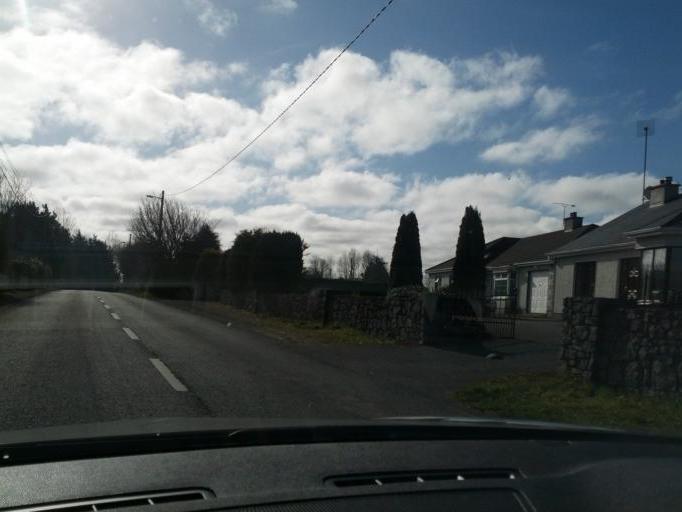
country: IE
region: Connaught
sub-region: County Galway
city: Ballinasloe
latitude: 53.3434
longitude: -8.2454
